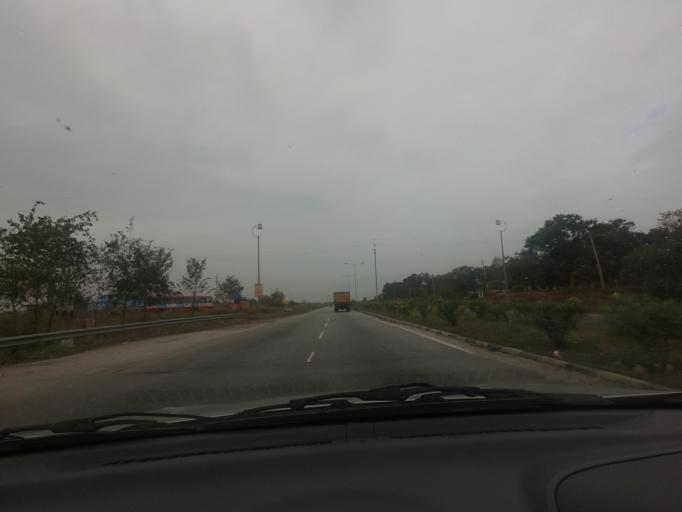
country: IN
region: Karnataka
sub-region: Tumkur
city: Kunigal
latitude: 13.0023
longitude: 76.9586
